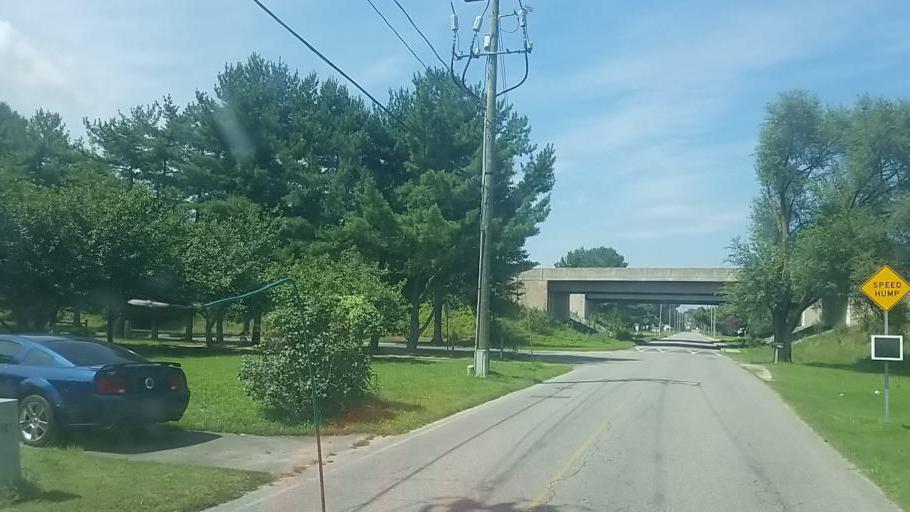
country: US
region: Maryland
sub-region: Caroline County
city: Denton
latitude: 38.8838
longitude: -75.8135
